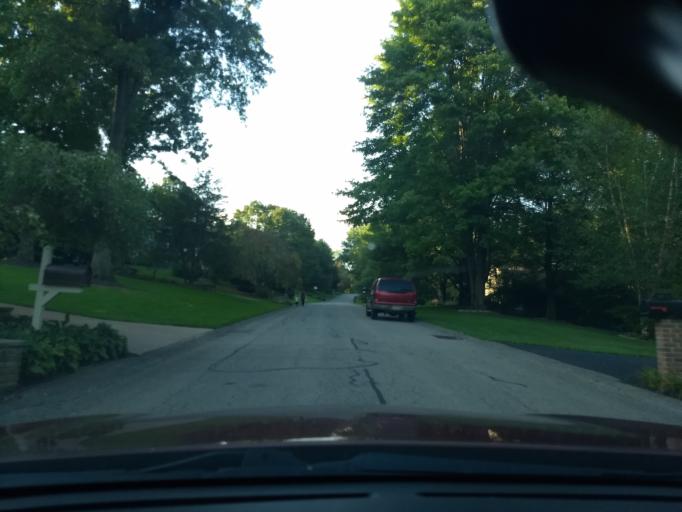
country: US
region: Pennsylvania
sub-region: Allegheny County
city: Gibsonia
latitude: 40.6407
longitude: -79.9630
